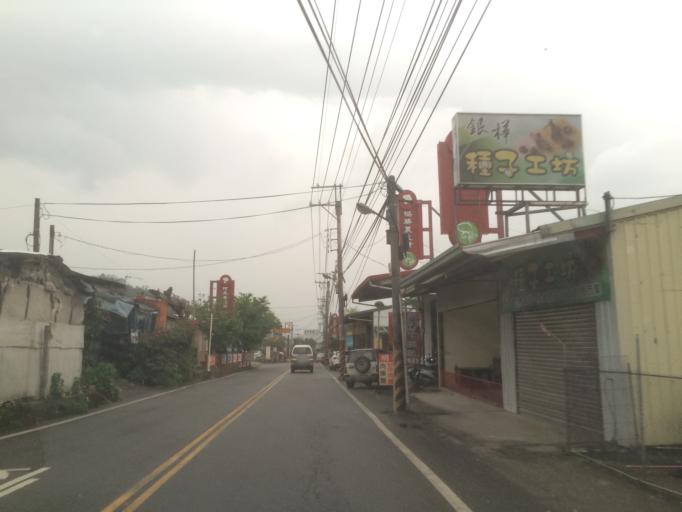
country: TW
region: Taiwan
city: Fengyuan
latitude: 24.1915
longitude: 120.8101
